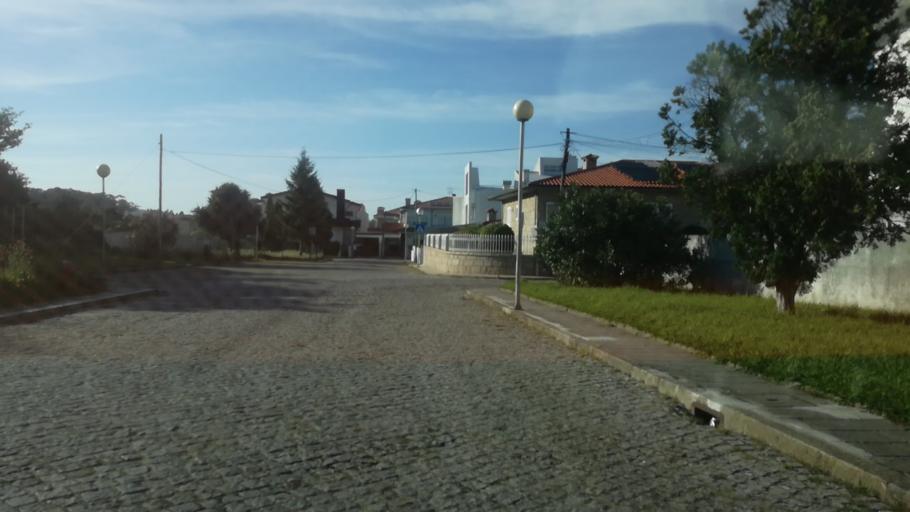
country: PT
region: Porto
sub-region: Maia
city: Gemunde
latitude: 41.2578
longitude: -8.6684
